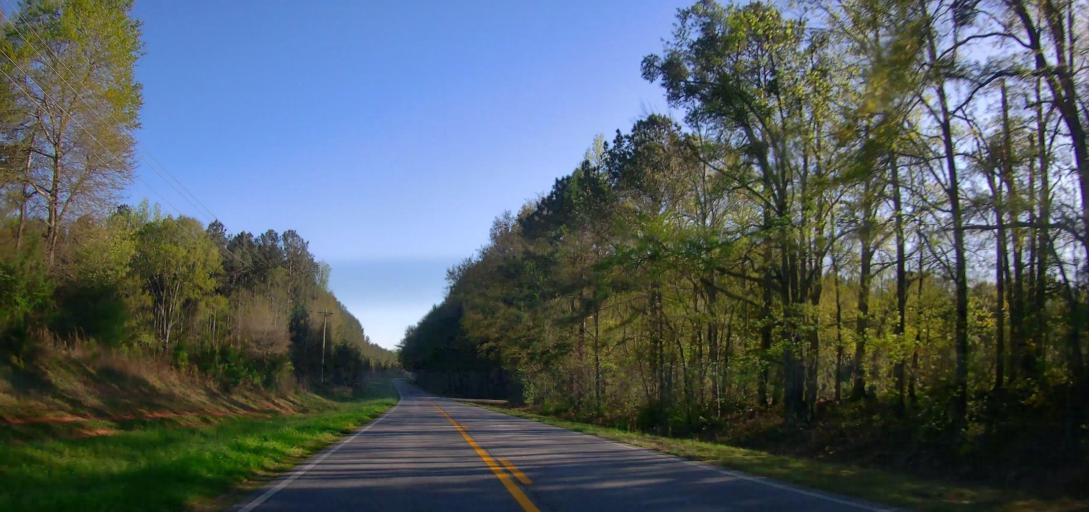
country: US
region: Georgia
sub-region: Butts County
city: Jackson
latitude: 33.3178
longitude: -83.9027
